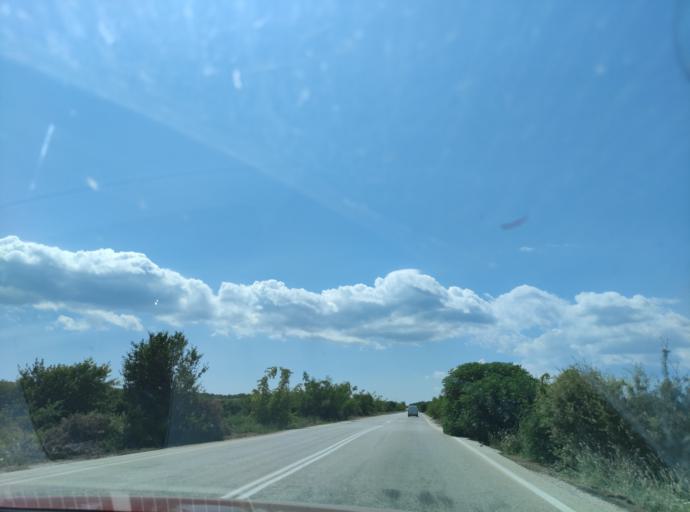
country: GR
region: East Macedonia and Thrace
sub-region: Nomos Kavalas
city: Nikisiani
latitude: 40.9909
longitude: 24.0836
